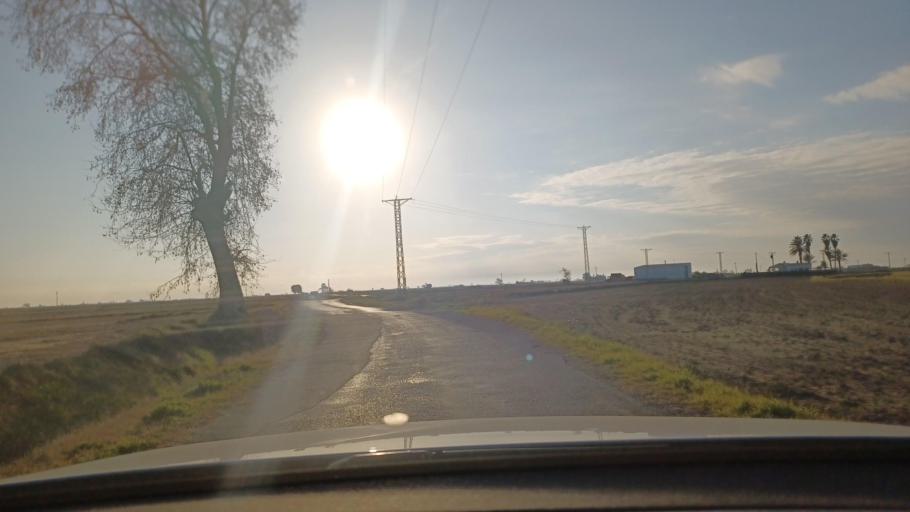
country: ES
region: Catalonia
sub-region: Provincia de Tarragona
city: Amposta
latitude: 40.7026
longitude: 0.6377
